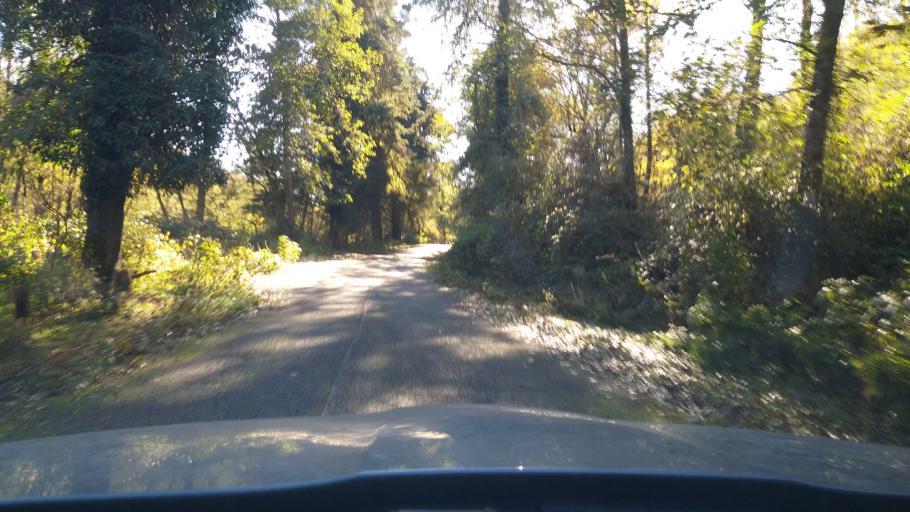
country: GE
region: Abkhazia
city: Bich'vinta
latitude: 43.1850
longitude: 40.4540
